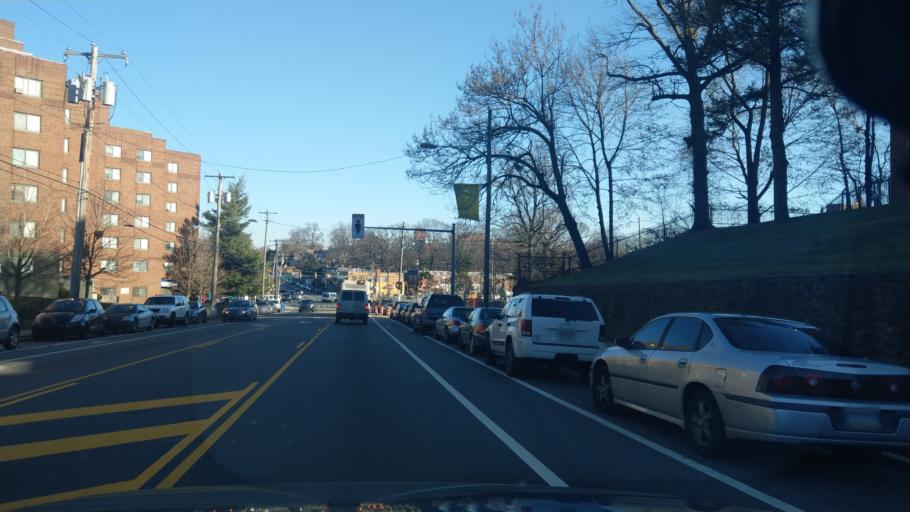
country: US
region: Pennsylvania
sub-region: Montgomery County
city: Wyncote
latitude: 40.0392
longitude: -75.1520
